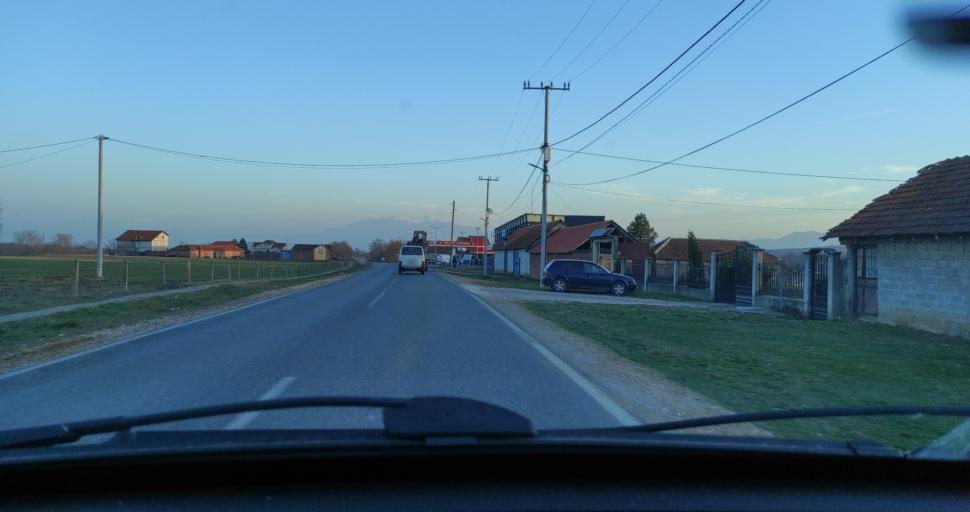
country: XK
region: Gjakova
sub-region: Komuna e Decanit
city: Gllogjan
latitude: 42.4454
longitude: 20.3641
